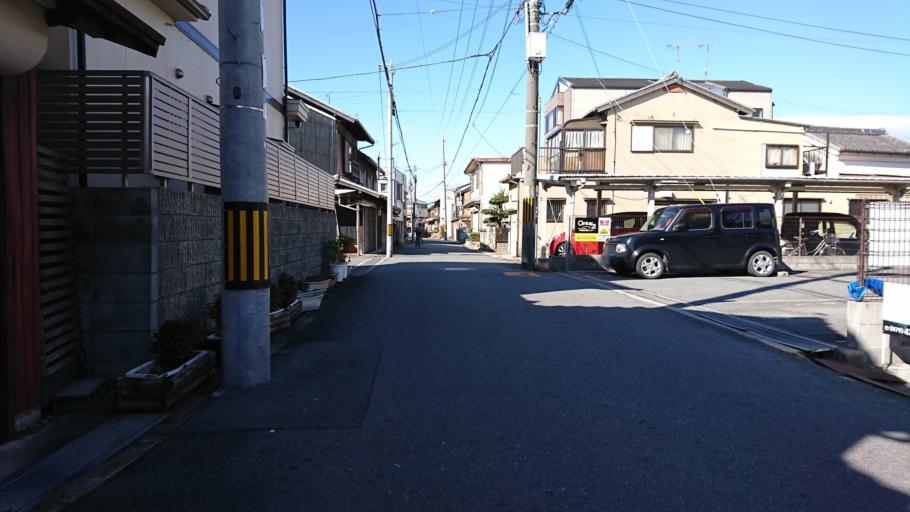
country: JP
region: Hyogo
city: Kakogawacho-honmachi
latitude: 34.7706
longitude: 134.8316
